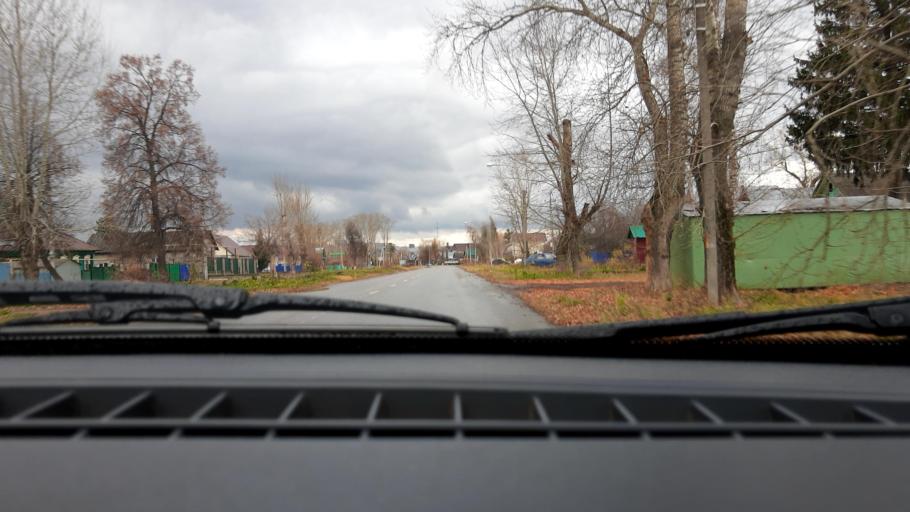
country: RU
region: Bashkortostan
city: Mikhaylovka
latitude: 54.7633
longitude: 55.8992
